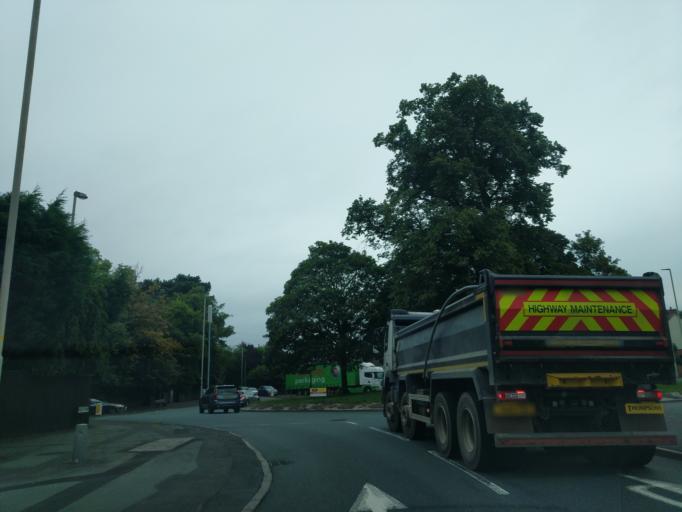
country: GB
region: England
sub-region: Worcestershire
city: Hagley
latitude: 52.4382
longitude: -2.1331
